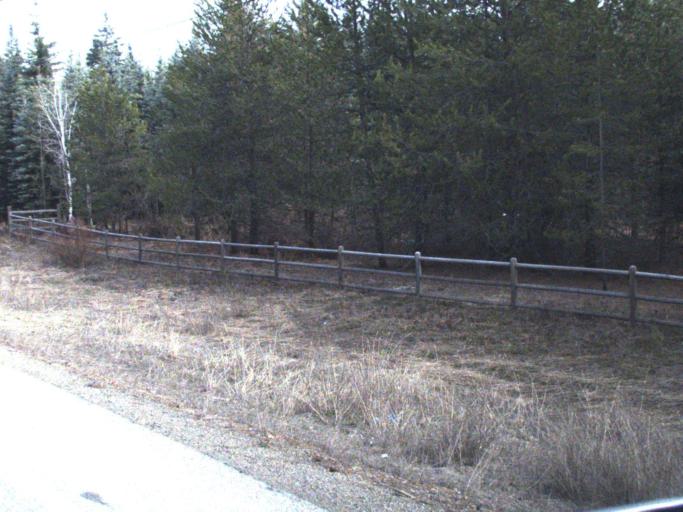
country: US
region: Washington
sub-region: Pend Oreille County
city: Newport
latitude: 48.2653
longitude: -117.2570
